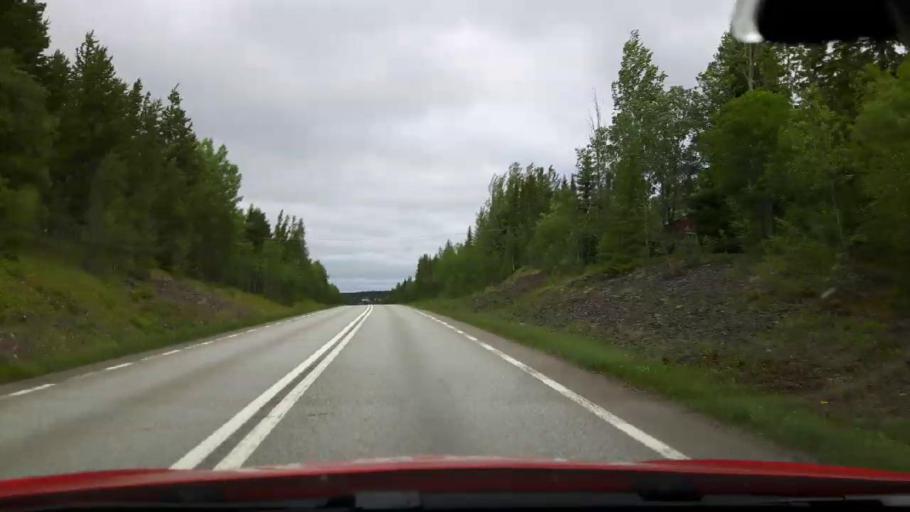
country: SE
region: Jaemtland
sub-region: Krokoms Kommun
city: Krokom
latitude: 63.5012
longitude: 14.5135
